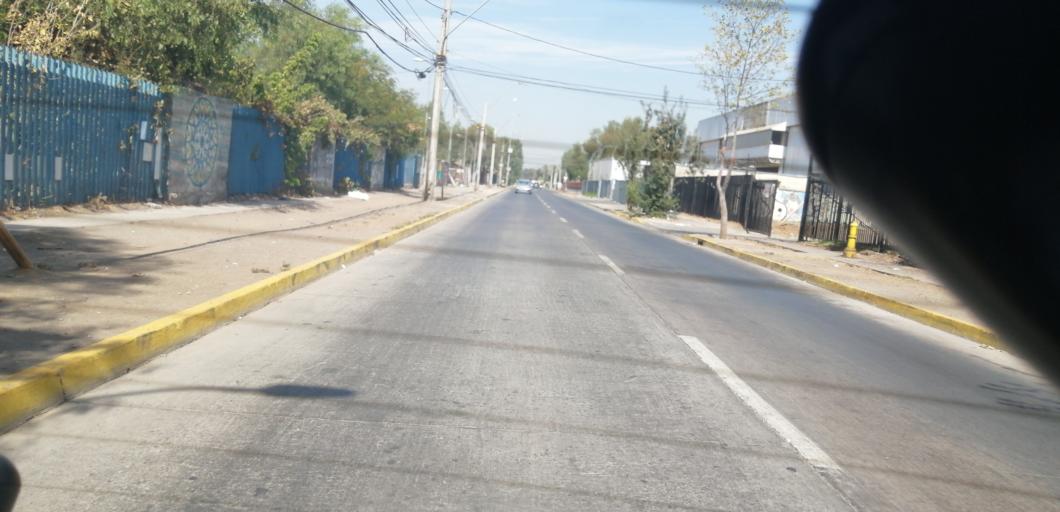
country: CL
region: Santiago Metropolitan
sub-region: Provincia de Santiago
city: Lo Prado
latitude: -33.4557
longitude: -70.7448
